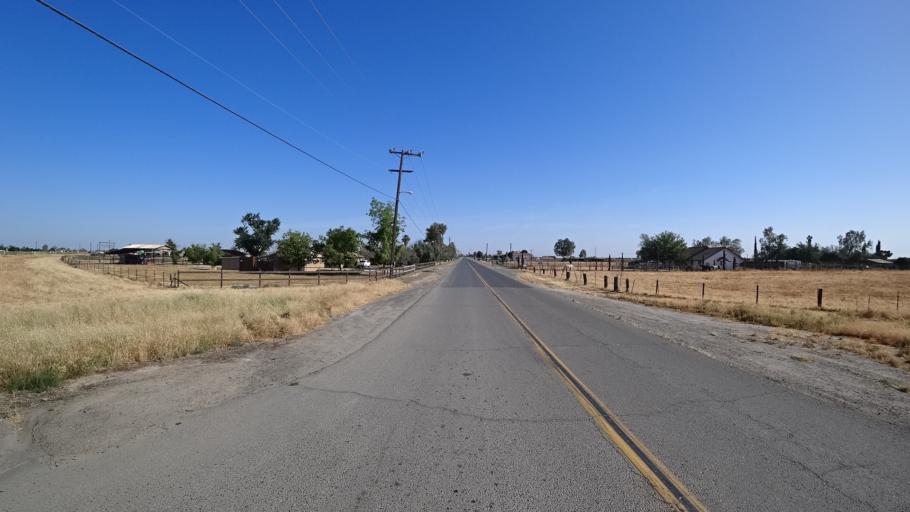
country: US
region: California
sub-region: Kings County
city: Corcoran
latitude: 36.1107
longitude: -119.5632
